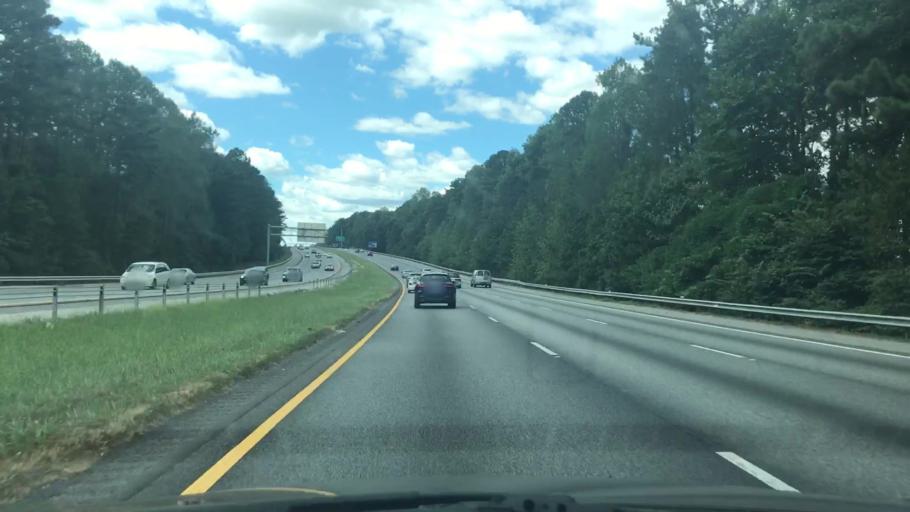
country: US
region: Georgia
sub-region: DeKalb County
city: Stone Mountain
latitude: 33.8310
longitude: -84.1821
